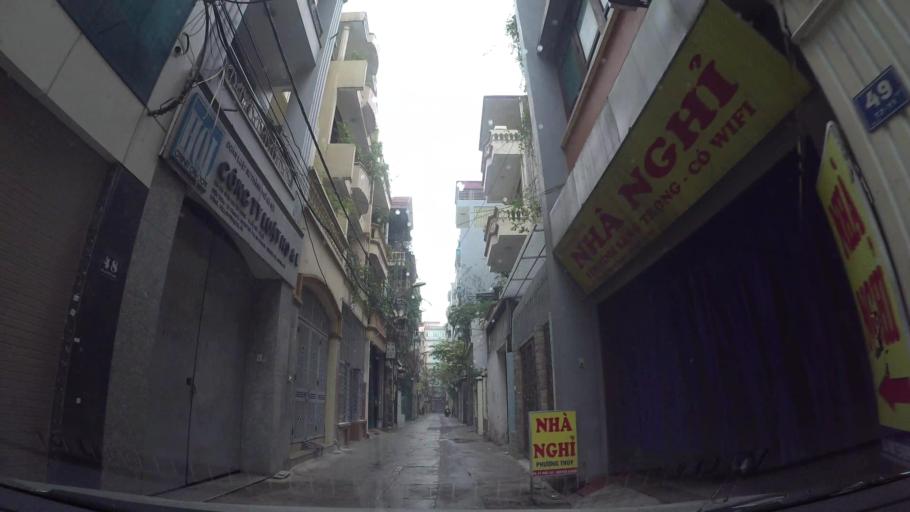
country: VN
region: Ha Noi
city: Cau Giay
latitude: 21.0199
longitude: 105.7997
